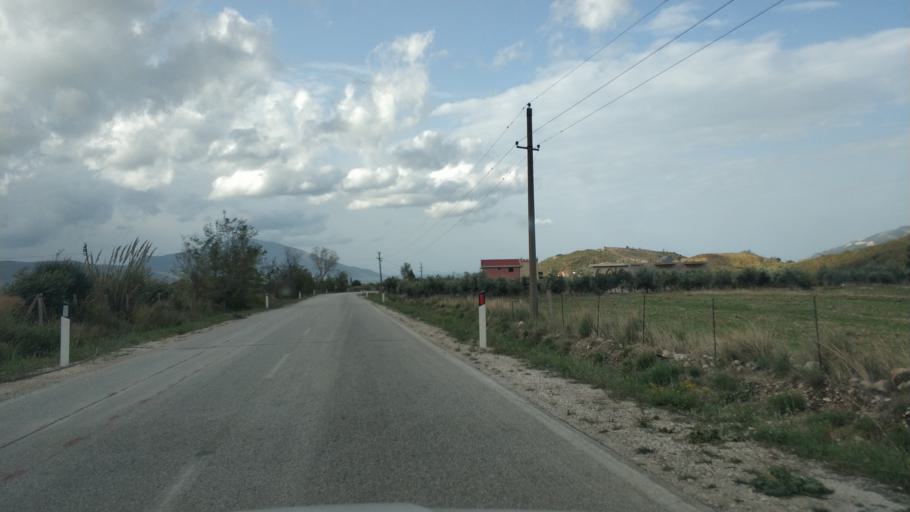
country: AL
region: Vlore
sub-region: Rrethi i Vlores
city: Orikum
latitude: 40.2875
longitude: 19.4946
